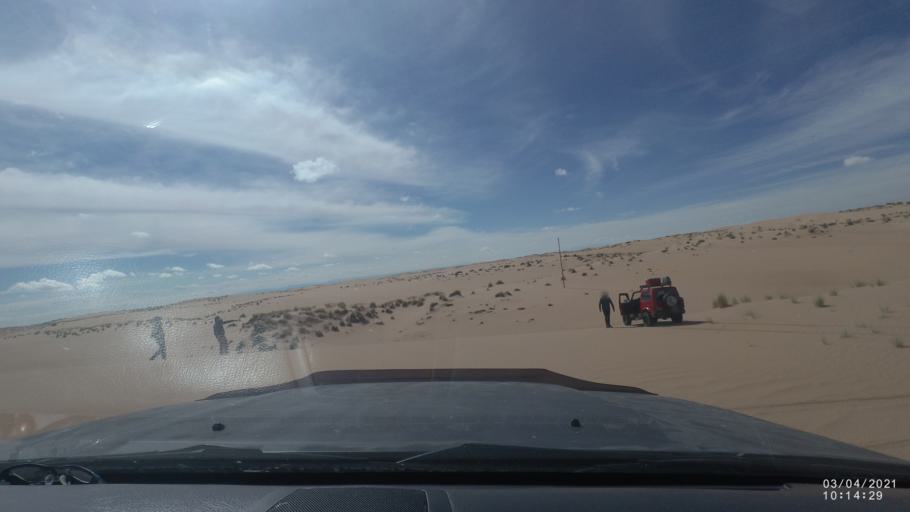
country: BO
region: Oruro
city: Poopo
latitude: -18.7043
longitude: -67.5261
